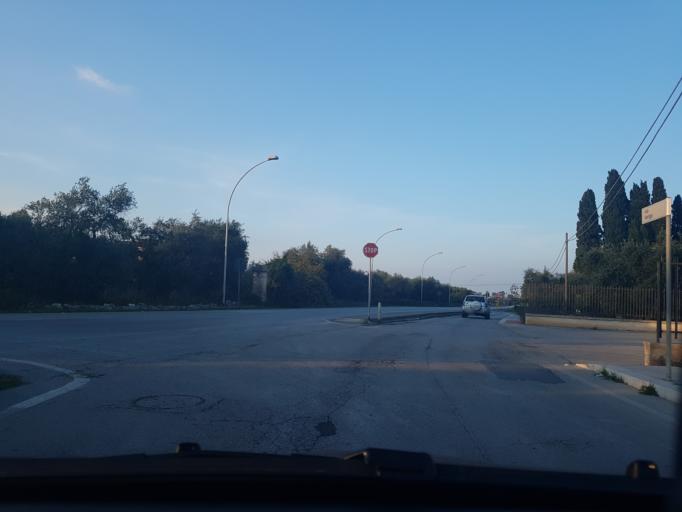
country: IT
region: Apulia
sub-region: Provincia di Bari
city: Bitritto
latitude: 41.0480
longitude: 16.8276
